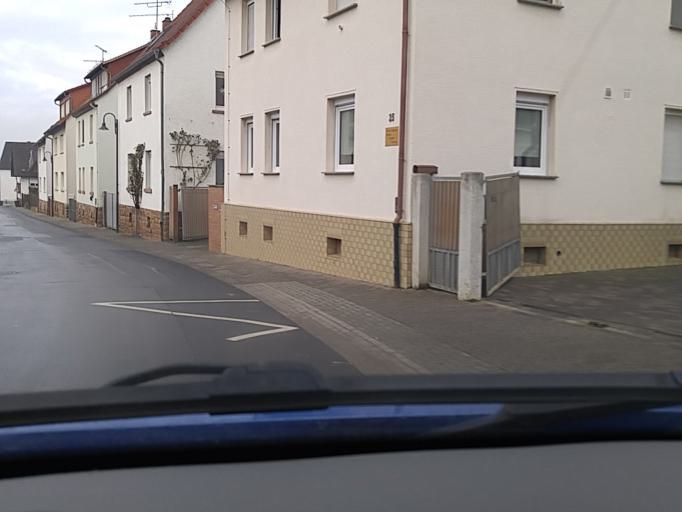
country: DE
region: Hesse
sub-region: Regierungsbezirk Darmstadt
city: Rockenberg
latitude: 50.4012
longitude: 8.7436
